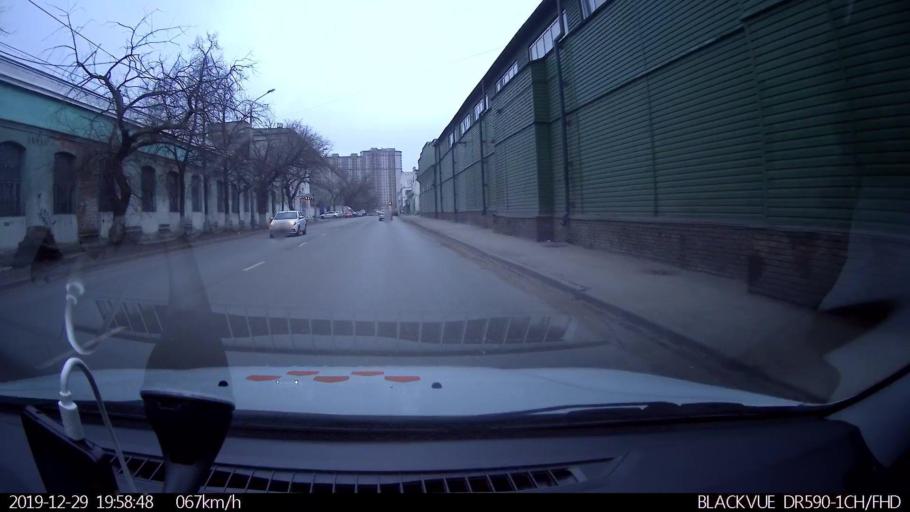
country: RU
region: Nizjnij Novgorod
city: Nizhniy Novgorod
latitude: 56.3131
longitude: 43.9503
